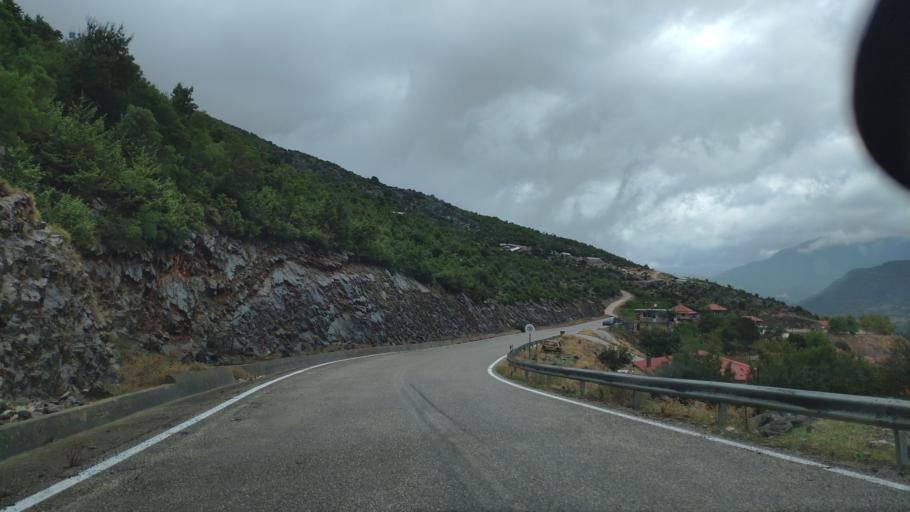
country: GR
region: Thessaly
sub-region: Nomos Kardhitsas
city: Anthiro
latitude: 39.1064
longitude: 21.4083
